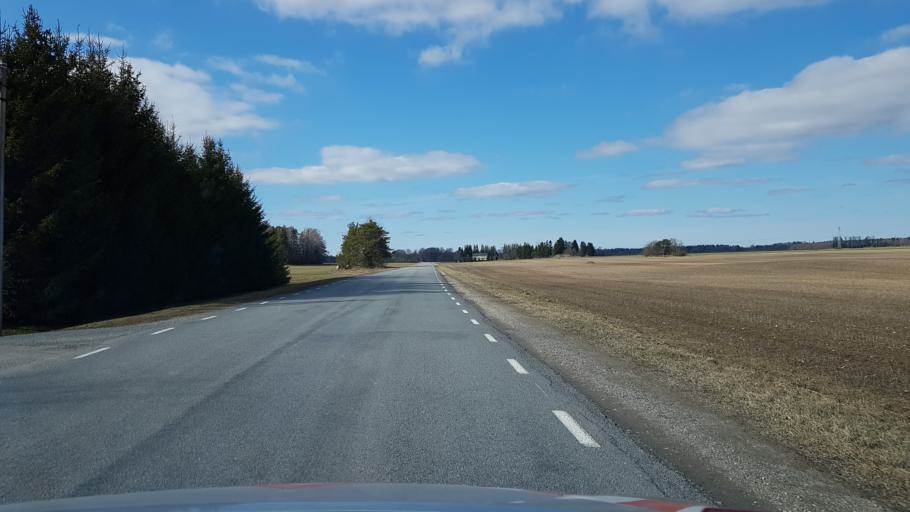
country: EE
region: Laeaene-Virumaa
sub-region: Tamsalu vald
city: Tamsalu
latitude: 59.1700
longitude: 26.0610
